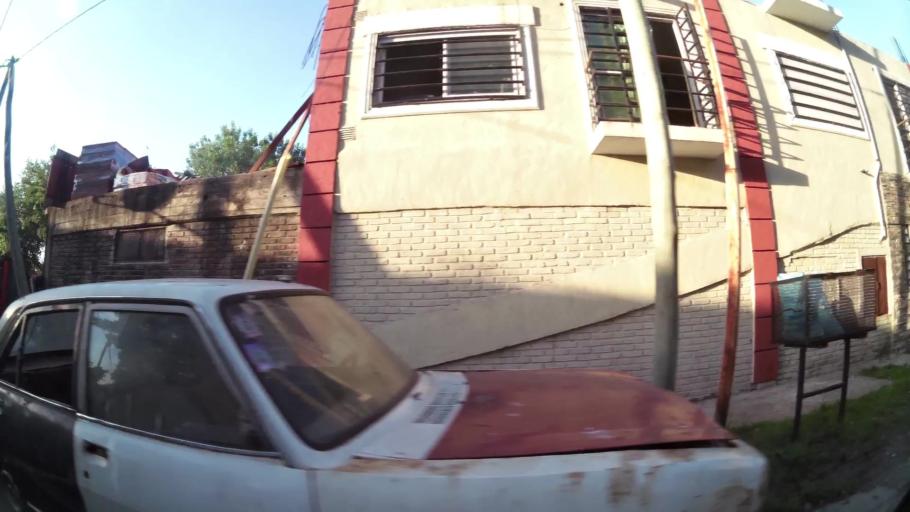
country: AR
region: Buenos Aires F.D.
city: Villa Lugano
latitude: -34.6977
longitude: -58.4808
